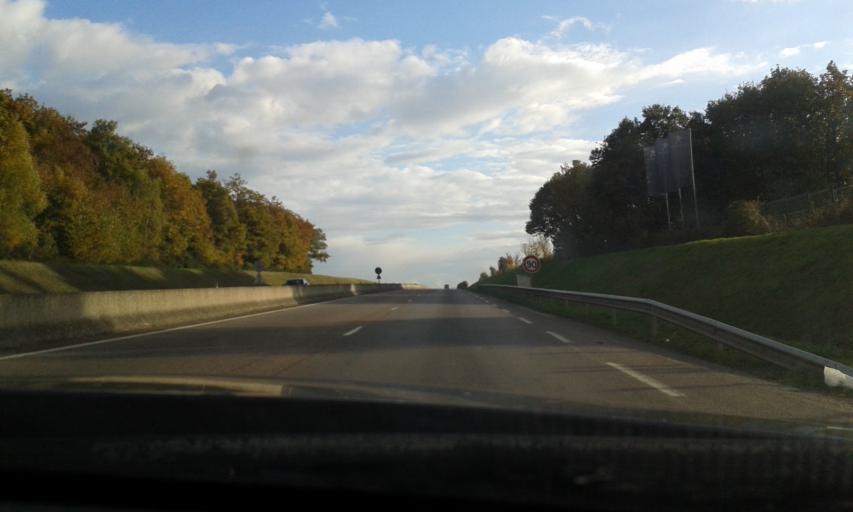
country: FR
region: Centre
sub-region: Departement d'Eure-et-Loir
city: Dreux
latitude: 48.7311
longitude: 1.3426
